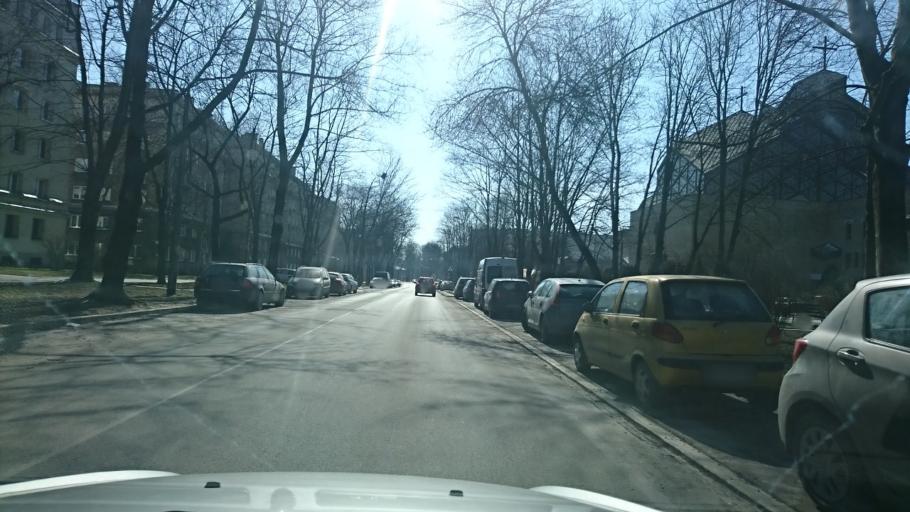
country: PL
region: Lesser Poland Voivodeship
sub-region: Powiat wielicki
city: Kokotow
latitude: 50.0766
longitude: 20.0456
